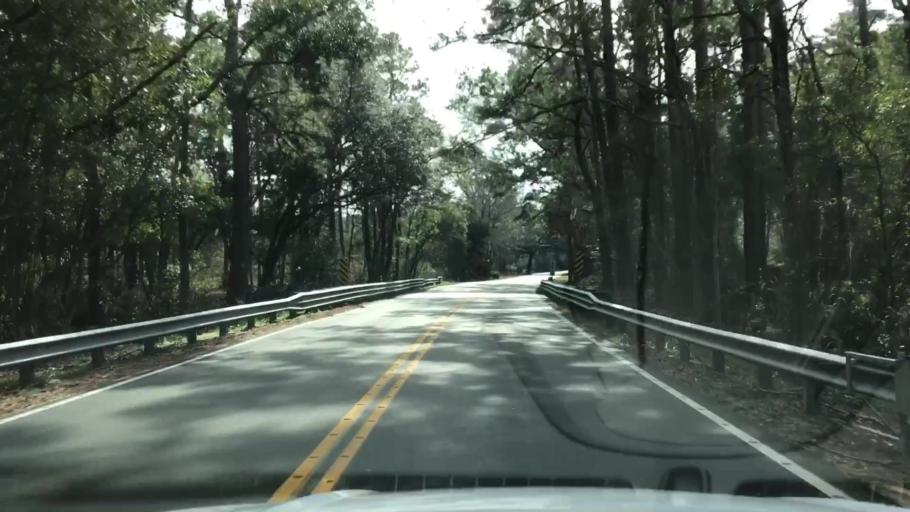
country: US
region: South Carolina
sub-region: Charleston County
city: Folly Beach
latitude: 32.7158
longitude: -80.0199
